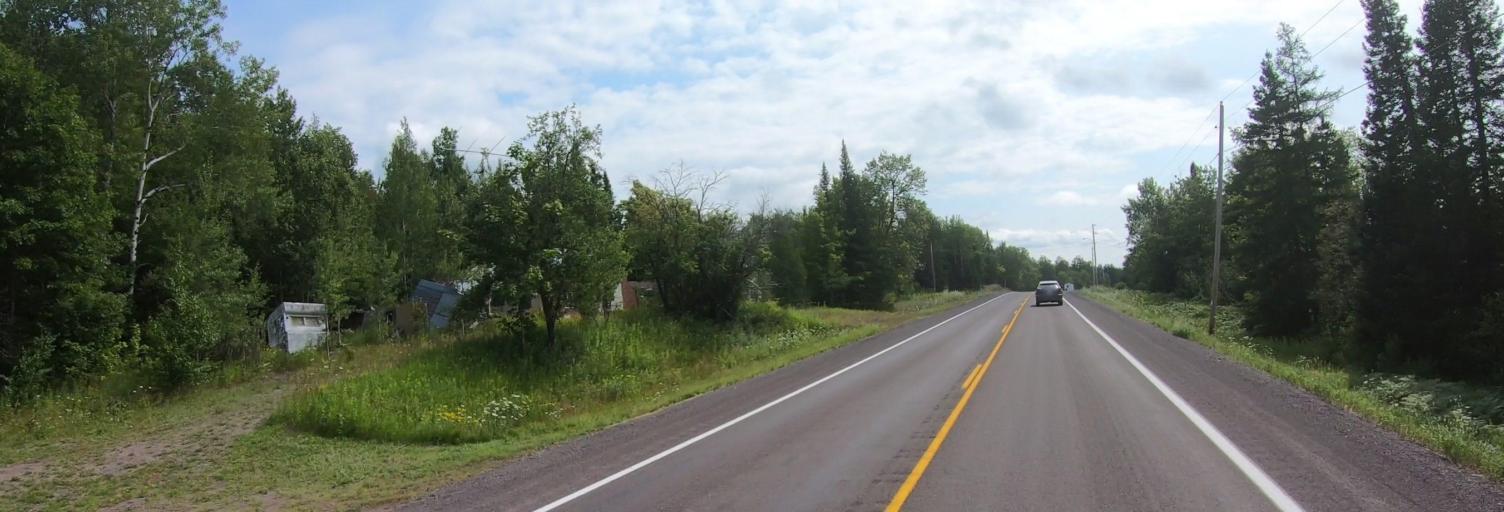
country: US
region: Michigan
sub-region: Houghton County
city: Hancock
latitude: 46.9427
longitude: -88.7911
